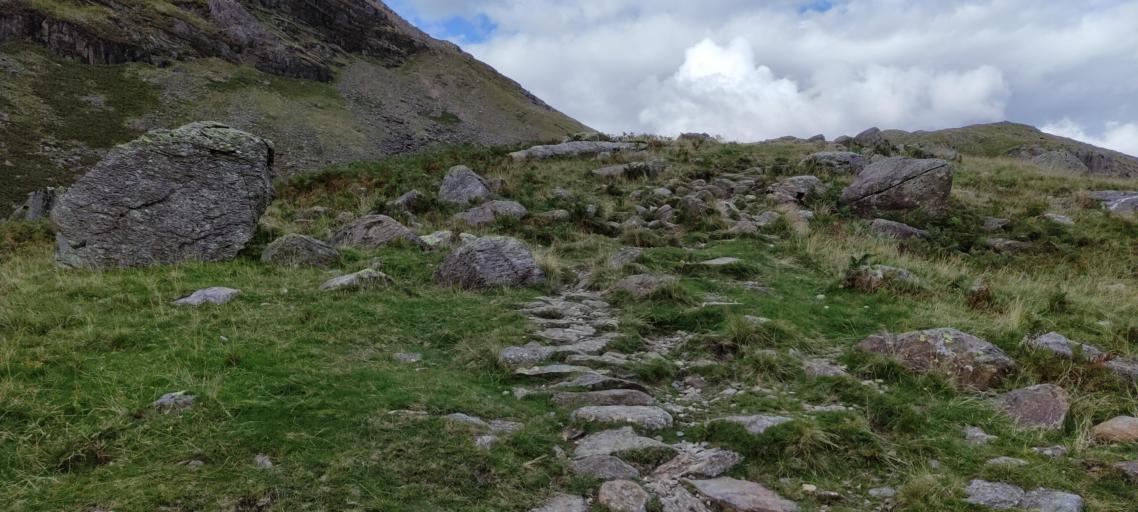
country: GB
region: England
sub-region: Cumbria
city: Ambleside
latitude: 54.3765
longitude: -3.1094
